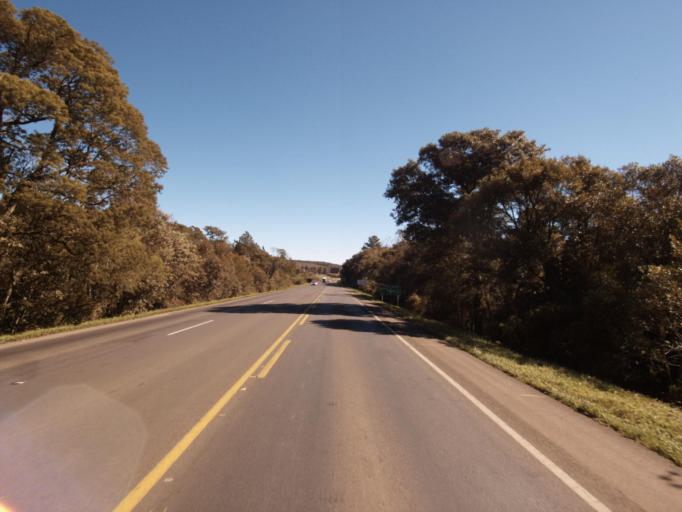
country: BR
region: Santa Catarina
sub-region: Concordia
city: Concordia
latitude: -26.9717
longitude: -51.8480
